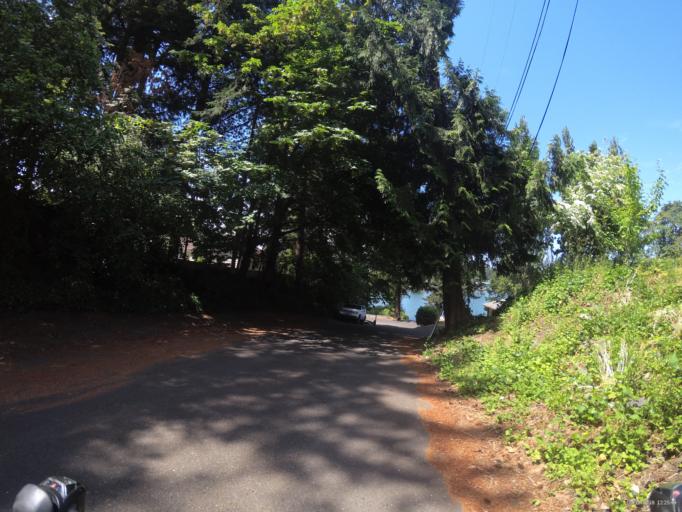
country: US
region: Washington
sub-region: Pierce County
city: Lakewood
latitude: 47.1737
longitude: -122.5335
